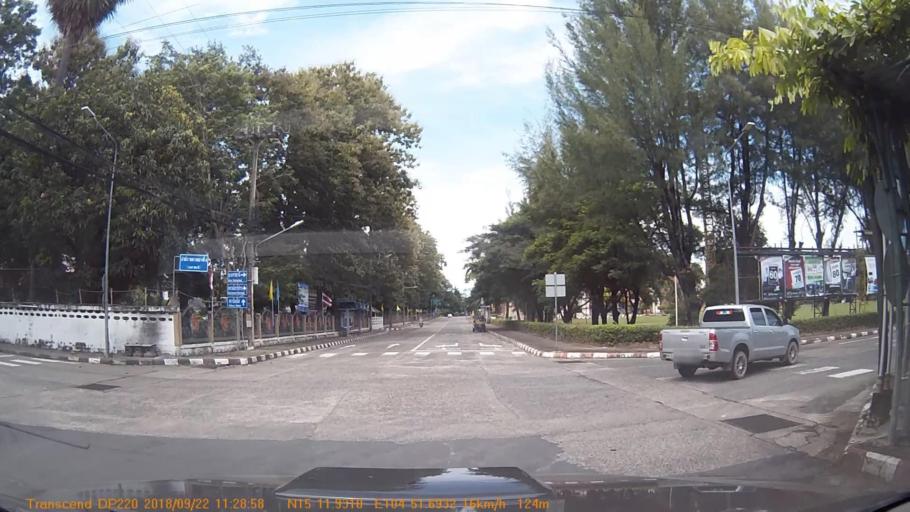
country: TH
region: Changwat Ubon Ratchathani
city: Warin Chamrap
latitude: 15.1989
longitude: 104.8615
